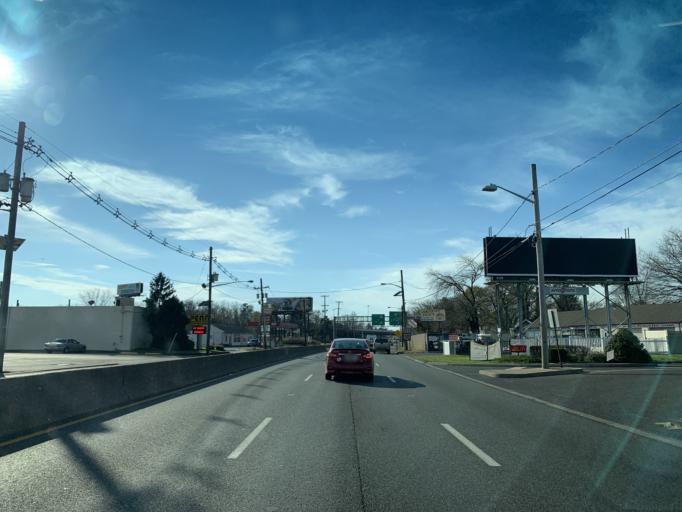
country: US
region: New Jersey
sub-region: Camden County
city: Merchantville
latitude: 39.9363
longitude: -75.0778
